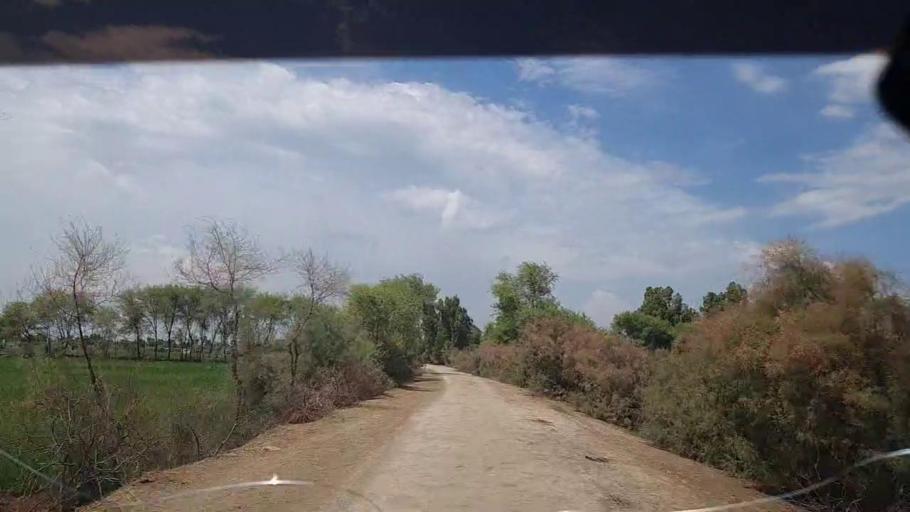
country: PK
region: Sindh
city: Ghauspur
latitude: 28.1499
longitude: 68.9974
